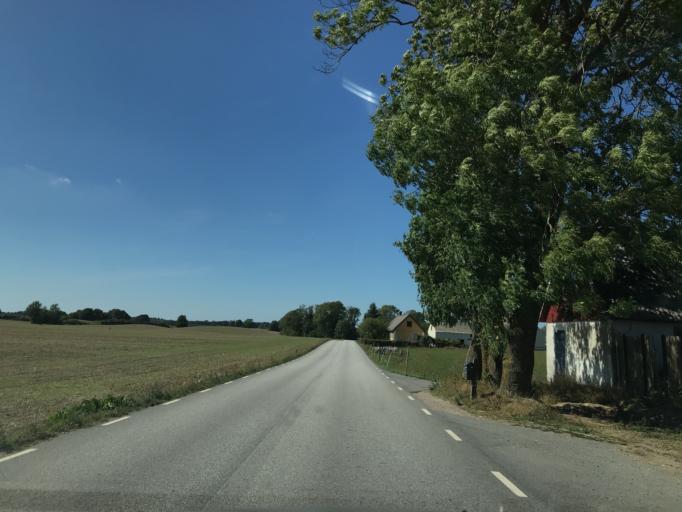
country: SE
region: Skane
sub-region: Tomelilla Kommun
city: Tomelilla
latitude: 55.6464
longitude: 13.9732
